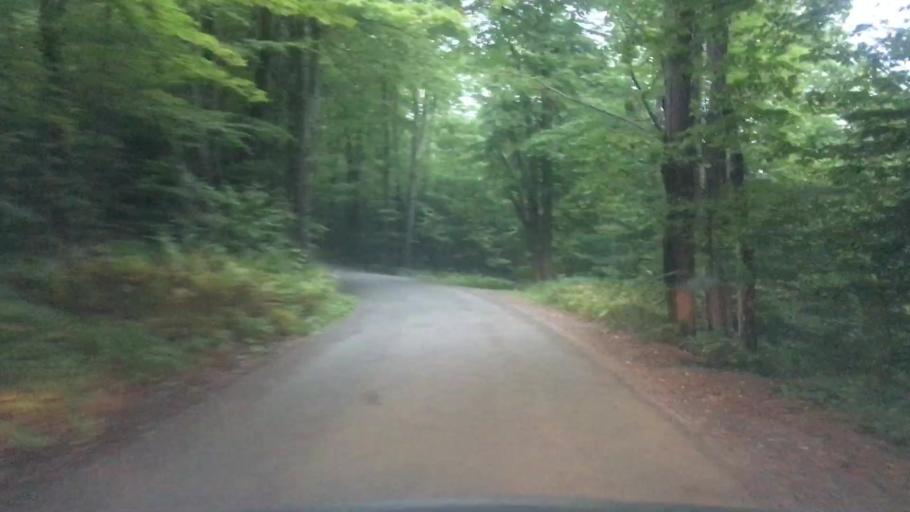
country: US
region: Vermont
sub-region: Windham County
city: Dover
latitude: 42.8471
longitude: -72.7719
